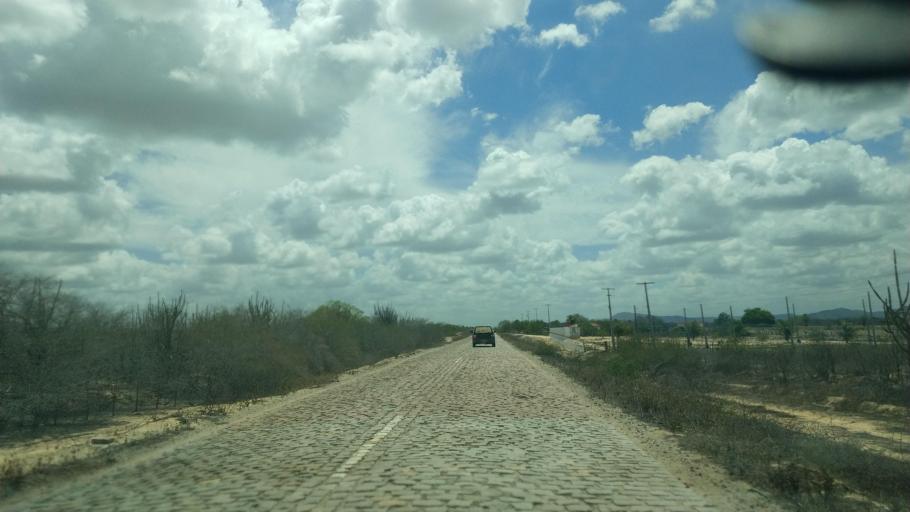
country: BR
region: Rio Grande do Norte
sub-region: Sao Paulo Do Potengi
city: Sao Paulo do Potengi
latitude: -5.9693
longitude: -35.8530
